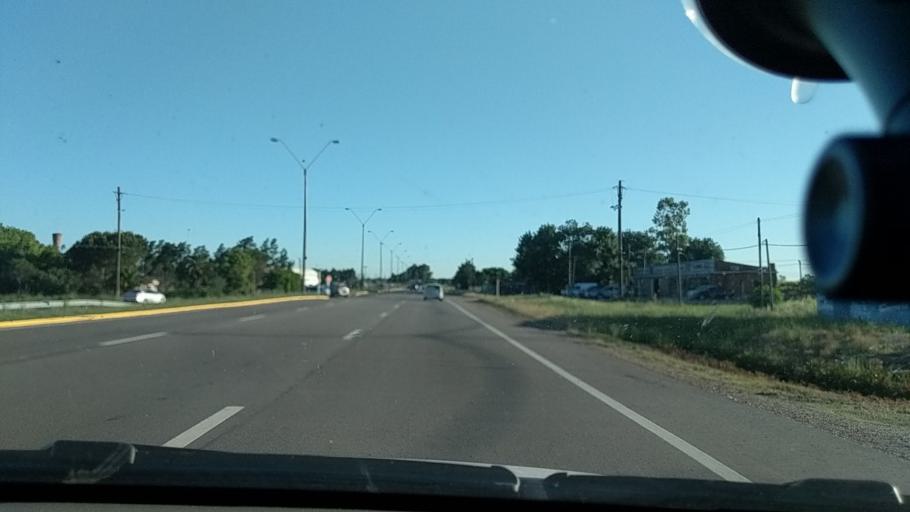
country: UY
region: Canelones
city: Joanico
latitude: -34.5950
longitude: -56.2623
